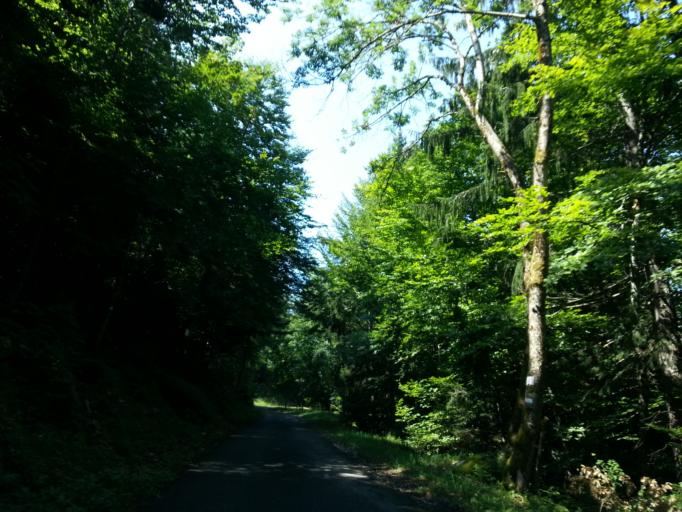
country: FR
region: Rhone-Alpes
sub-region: Departement de la Haute-Savoie
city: Veyrier-du-Lac
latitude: 45.9106
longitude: 6.1805
